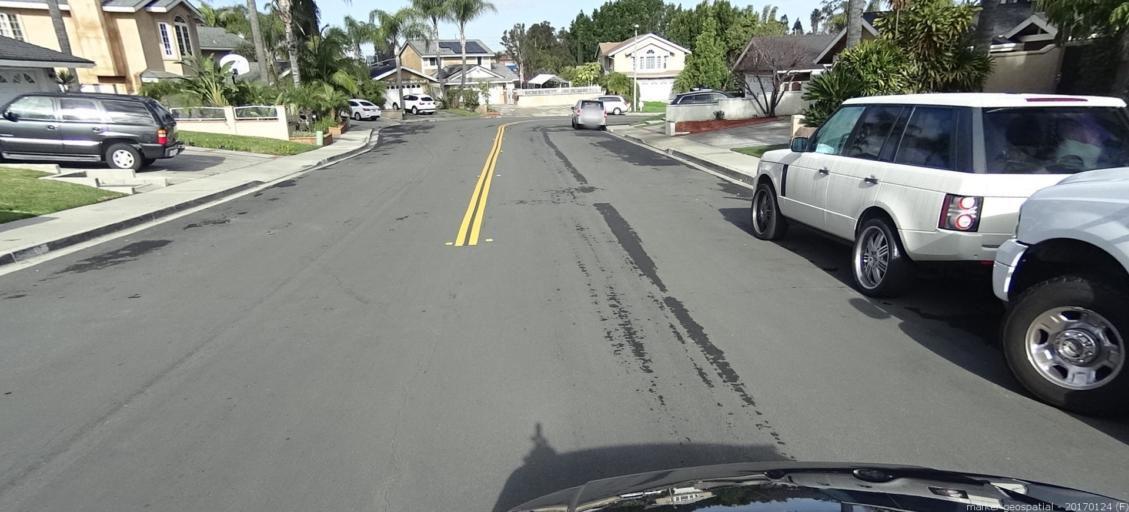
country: US
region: California
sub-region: Orange County
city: Laguna Hills
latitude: 33.6283
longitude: -117.7154
